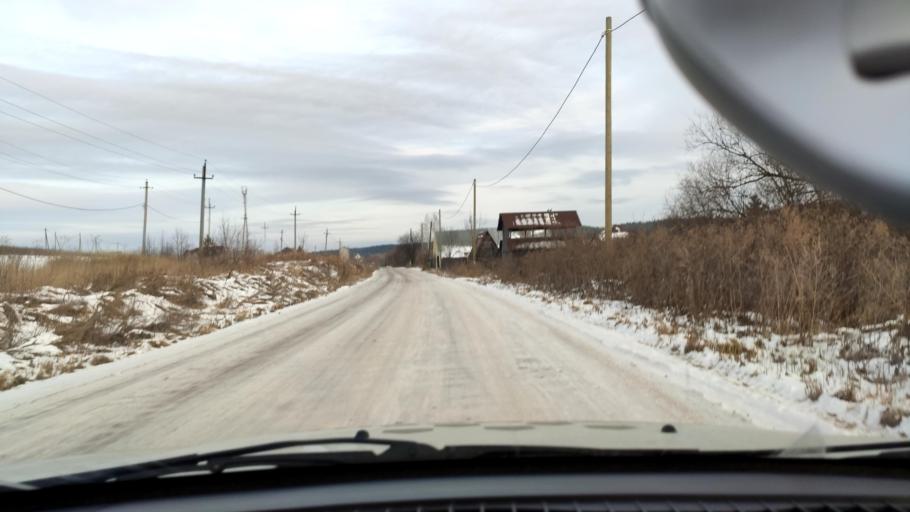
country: RU
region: Perm
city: Lobanovo
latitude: 57.8326
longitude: 56.3664
